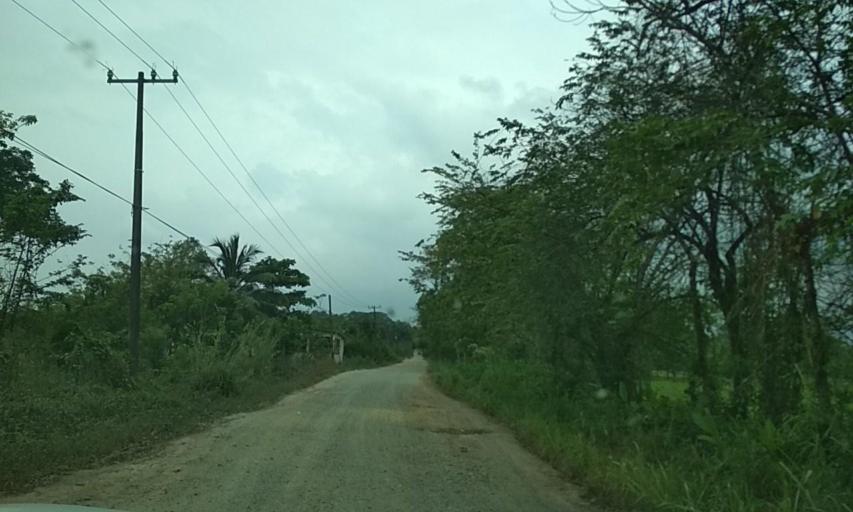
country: MX
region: Veracruz
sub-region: Uxpanapa
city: Poblado 10
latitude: 17.5015
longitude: -94.1497
